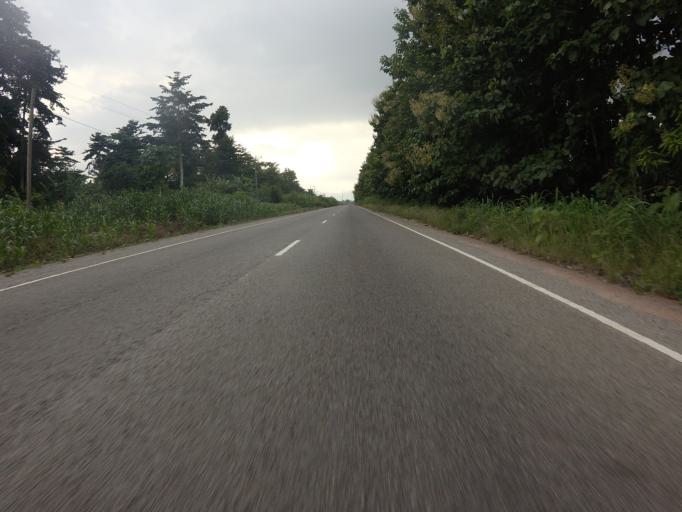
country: GH
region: Volta
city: Ho
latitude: 6.7779
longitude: 0.4714
